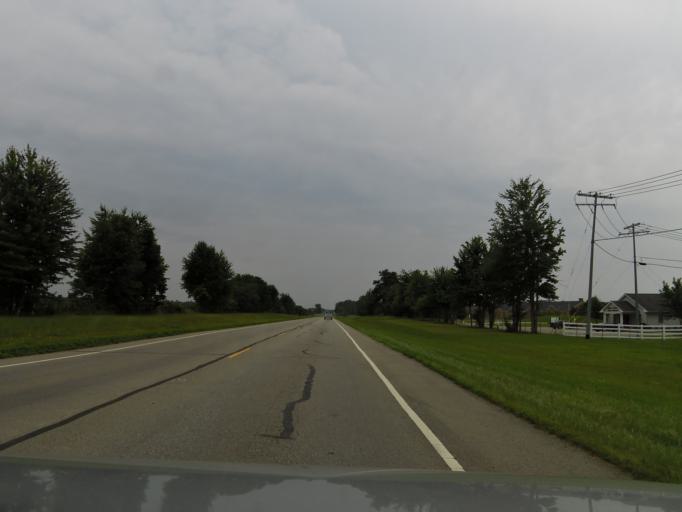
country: US
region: Ohio
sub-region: Brown County
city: Georgetown
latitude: 38.8785
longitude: -83.8883
